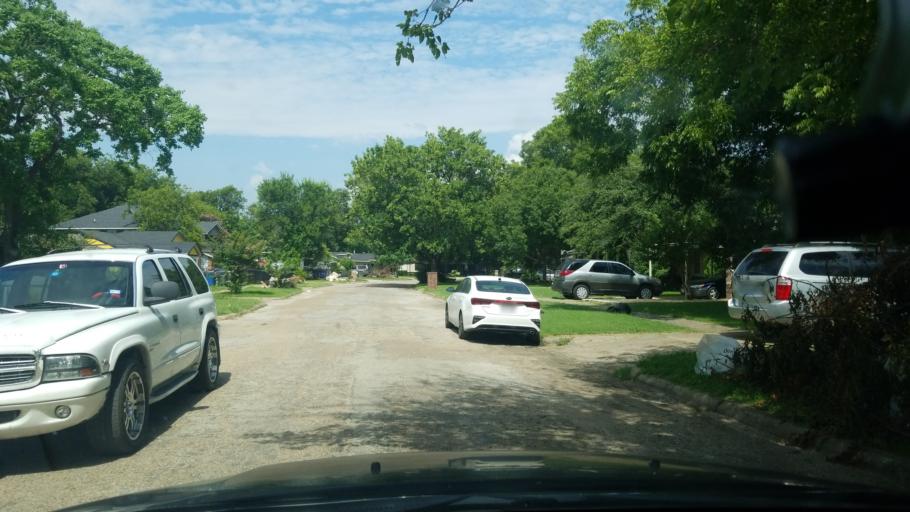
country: US
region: Texas
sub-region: Dallas County
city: Balch Springs
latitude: 32.7379
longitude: -96.6869
